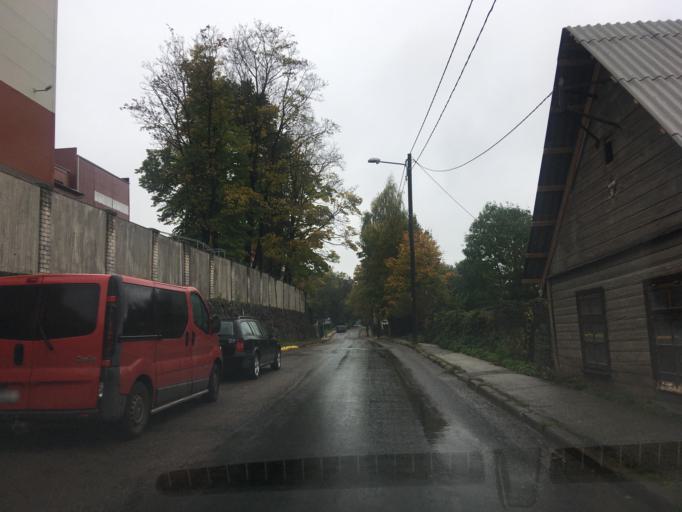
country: EE
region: Tartu
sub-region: Tartu linn
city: Tartu
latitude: 58.3864
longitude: 26.7078
